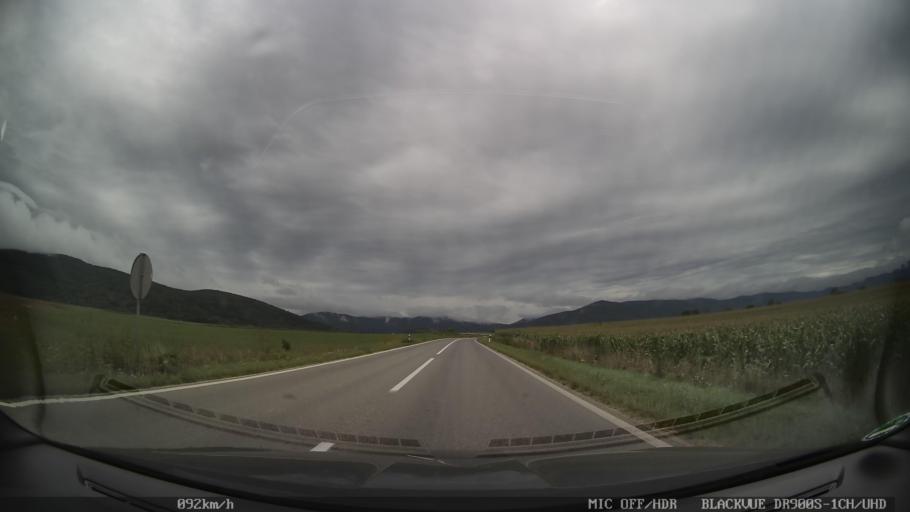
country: HR
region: Licko-Senjska
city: Otocac
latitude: 44.8561
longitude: 15.2773
